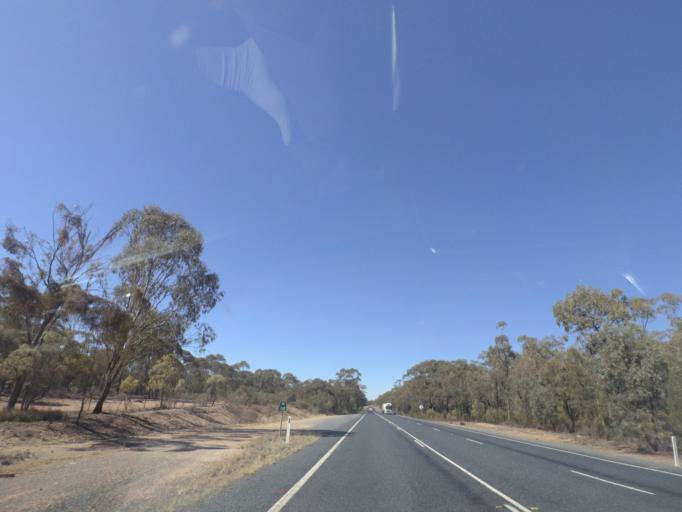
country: AU
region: New South Wales
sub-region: Bland
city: West Wyalong
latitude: -34.1327
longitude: 147.1229
